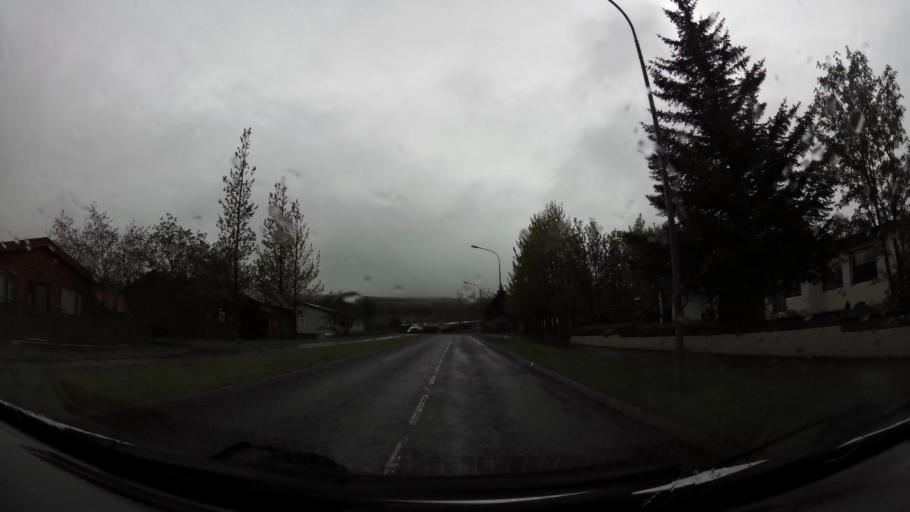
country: IS
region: South
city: Hveragerdi
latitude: 64.0023
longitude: -21.2001
